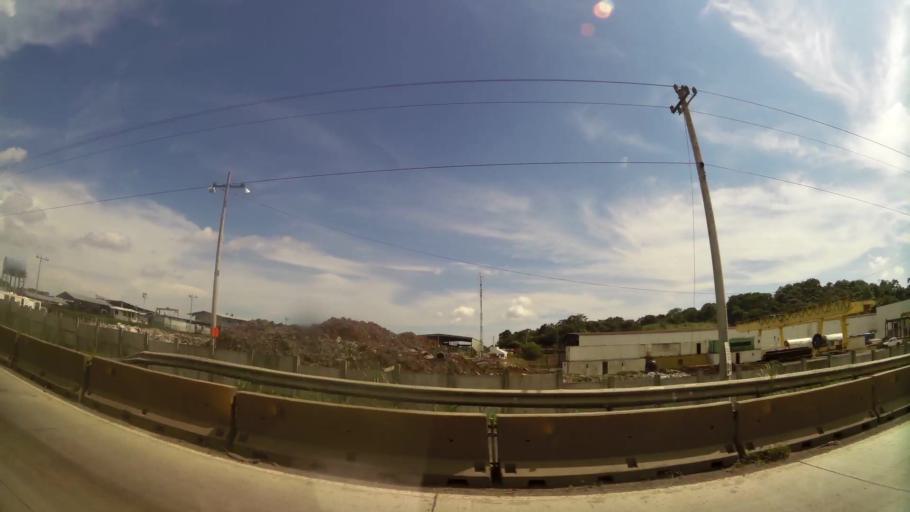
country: PA
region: Panama
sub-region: Distrito de Panama
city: Paraiso
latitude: 9.0304
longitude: -79.5849
